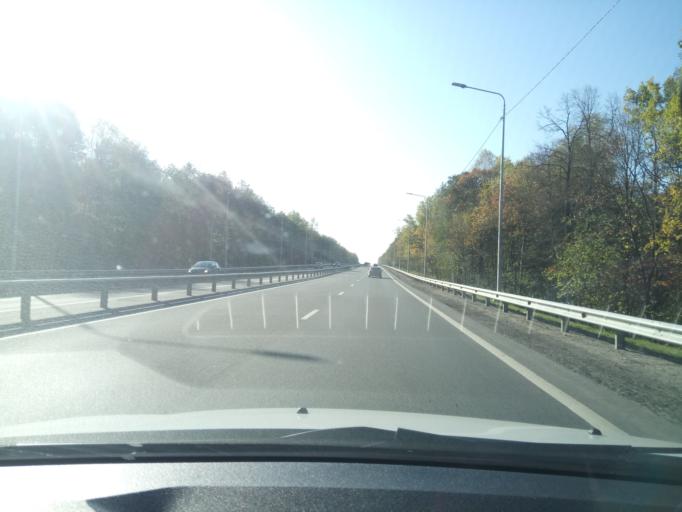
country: RU
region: Nizjnij Novgorod
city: Burevestnik
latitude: 56.0268
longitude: 43.9626
